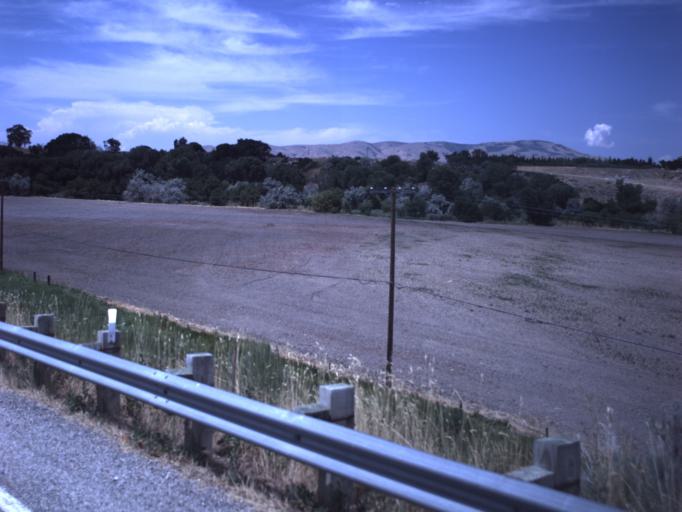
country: US
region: Utah
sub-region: Box Elder County
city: Elwood
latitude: 41.7141
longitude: -112.1117
